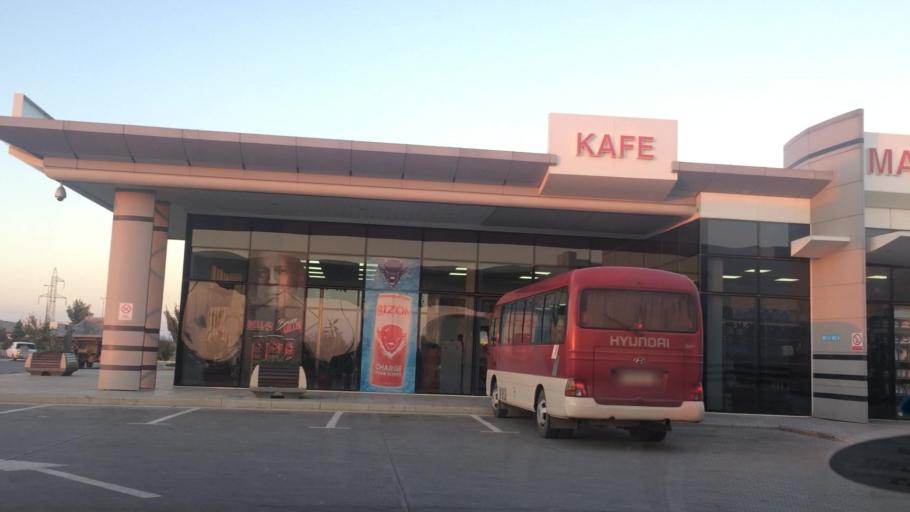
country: AZ
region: Baki
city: Qobustan
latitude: 39.9701
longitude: 49.4156
